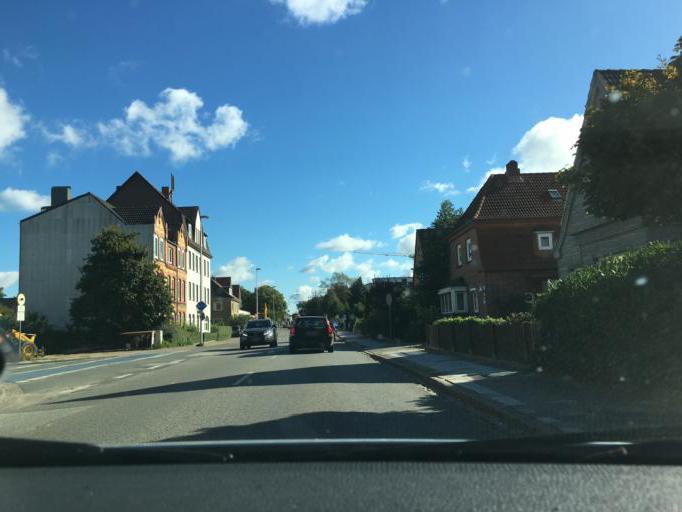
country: DE
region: Schleswig-Holstein
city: Kronshagen
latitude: 54.3320
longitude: 10.0797
